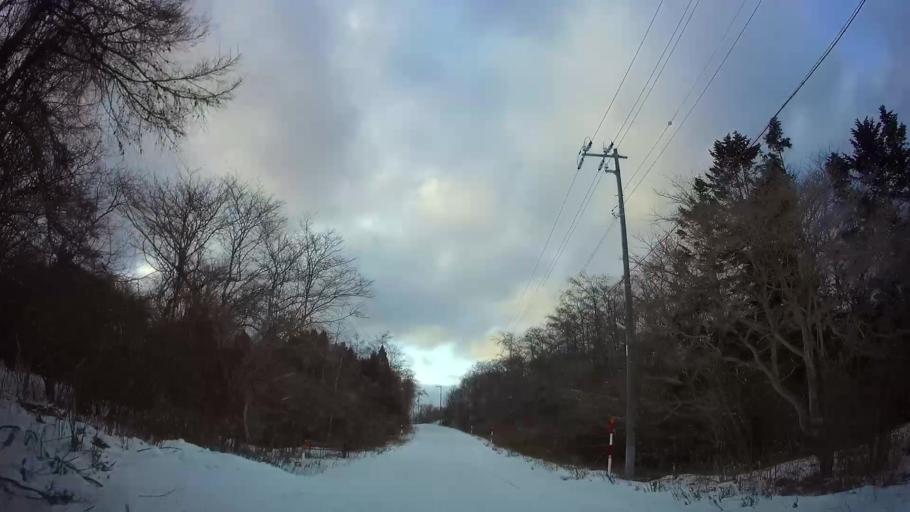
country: JP
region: Hokkaido
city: Nanae
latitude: 42.0197
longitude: 140.8416
